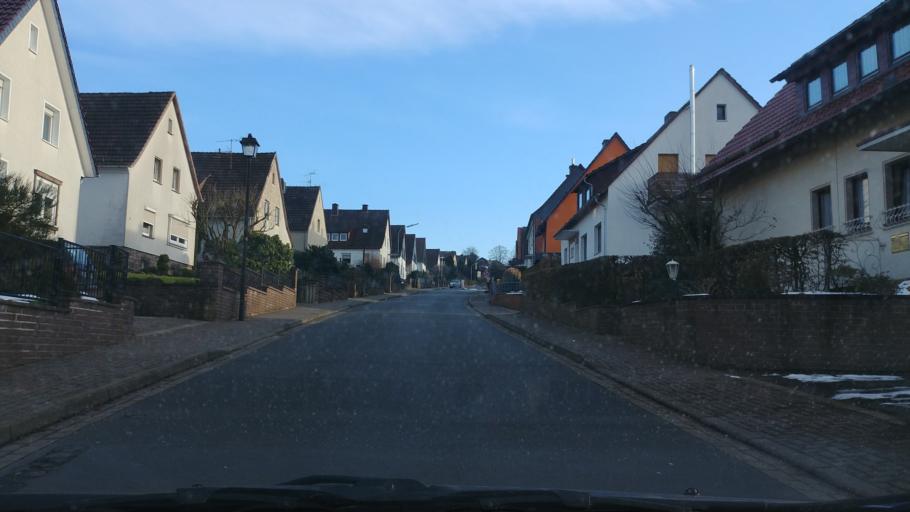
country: DE
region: Lower Saxony
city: Uslar
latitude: 51.6560
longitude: 9.6368
